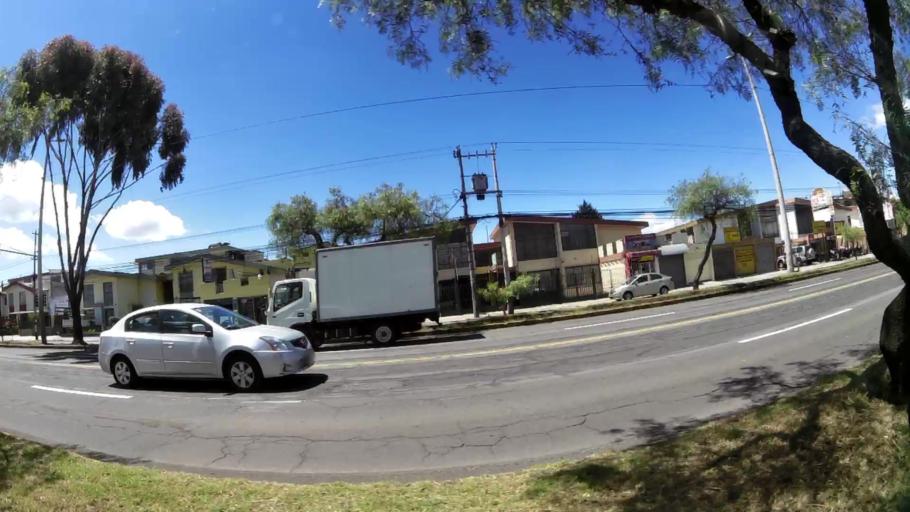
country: EC
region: Pichincha
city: Quito
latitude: -0.1462
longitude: -78.4836
